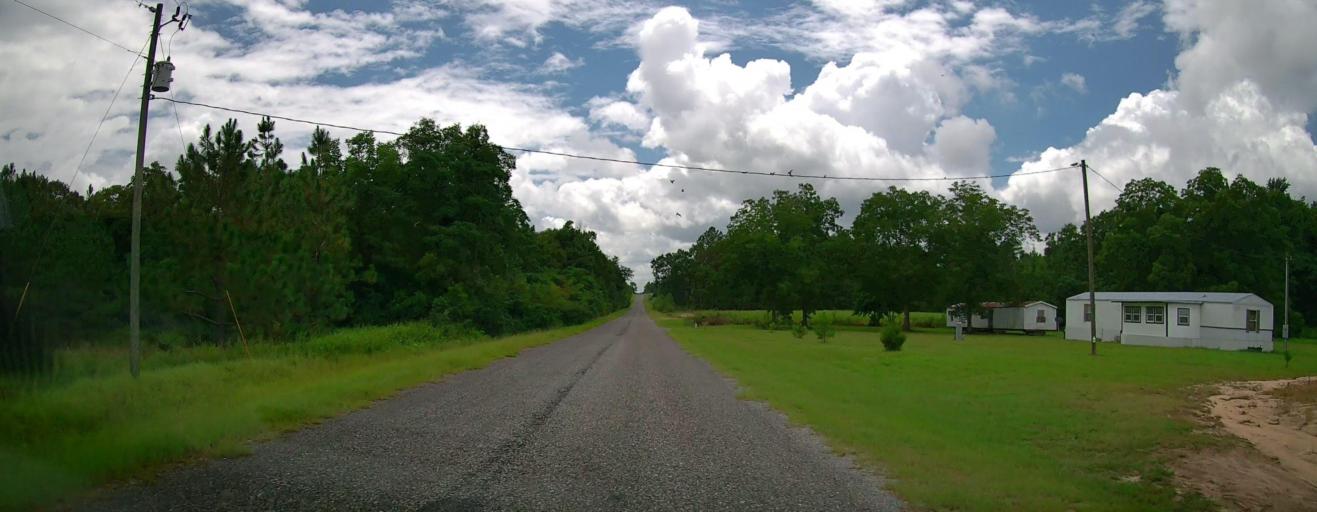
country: US
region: Georgia
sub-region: Dooly County
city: Vienna
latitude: 32.0570
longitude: -83.6277
